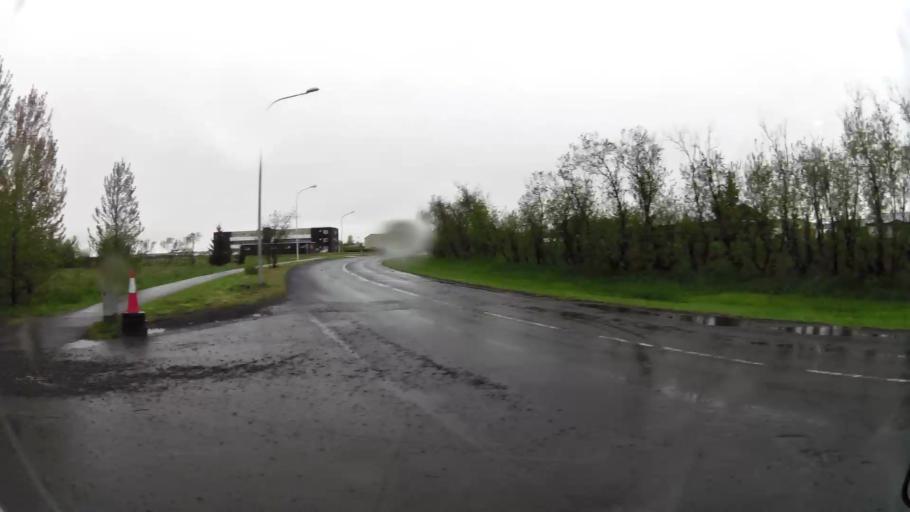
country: IS
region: South
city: Selfoss
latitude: 63.9310
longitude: -20.9793
